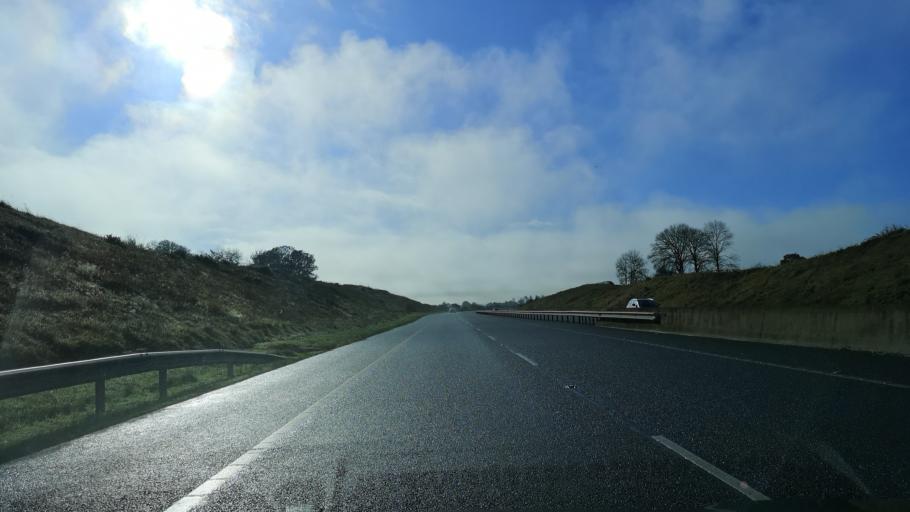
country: IE
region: Leinster
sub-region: An Iarmhi
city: Athlone
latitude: 53.3826
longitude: -8.0508
